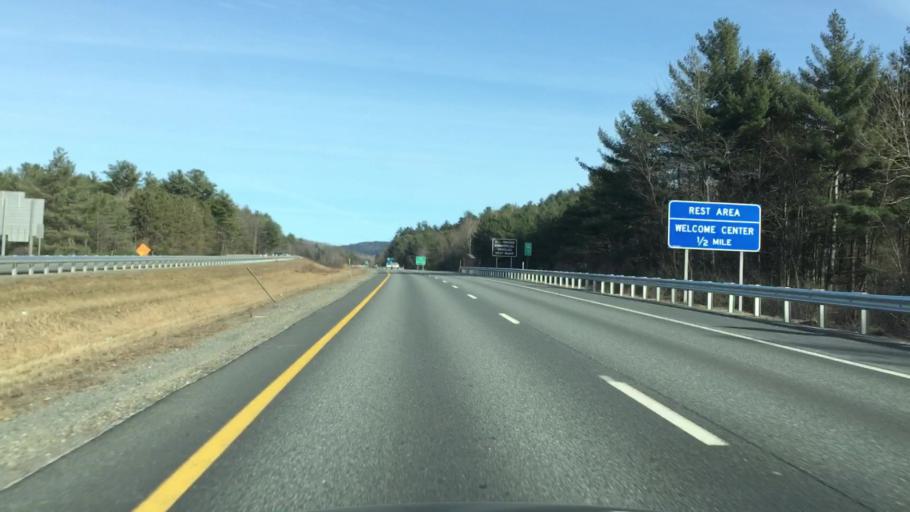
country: US
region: New Hampshire
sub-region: Grafton County
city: Lebanon
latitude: 43.6433
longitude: -72.2712
